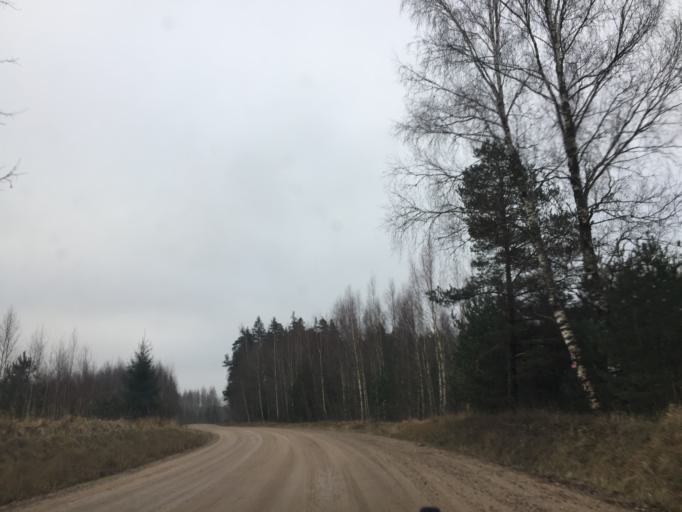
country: LV
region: Limbazu Rajons
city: Limbazi
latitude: 57.5900
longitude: 24.6376
